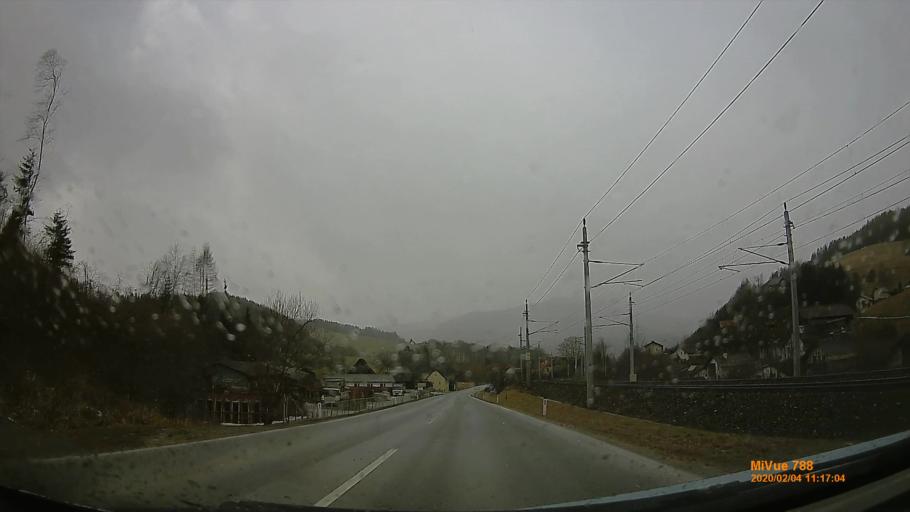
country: AT
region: Styria
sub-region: Politischer Bezirk Bruck-Muerzzuschlag
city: Muerzzuschlag
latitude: 47.6048
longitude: 15.7068
